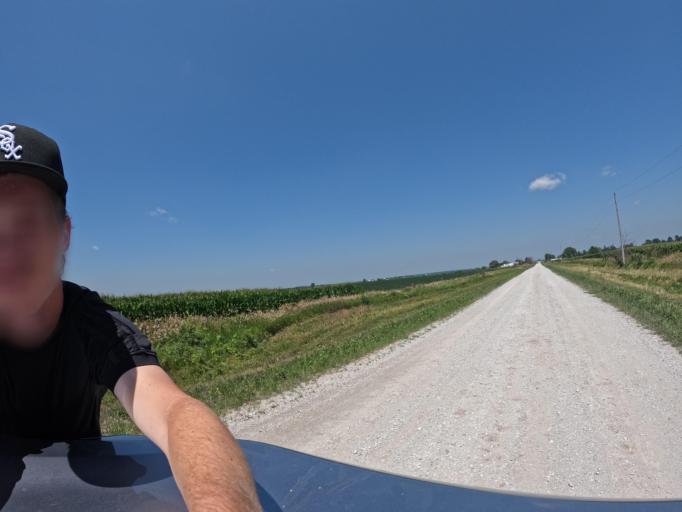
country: US
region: Iowa
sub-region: Keokuk County
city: Sigourney
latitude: 41.2648
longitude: -92.1699
